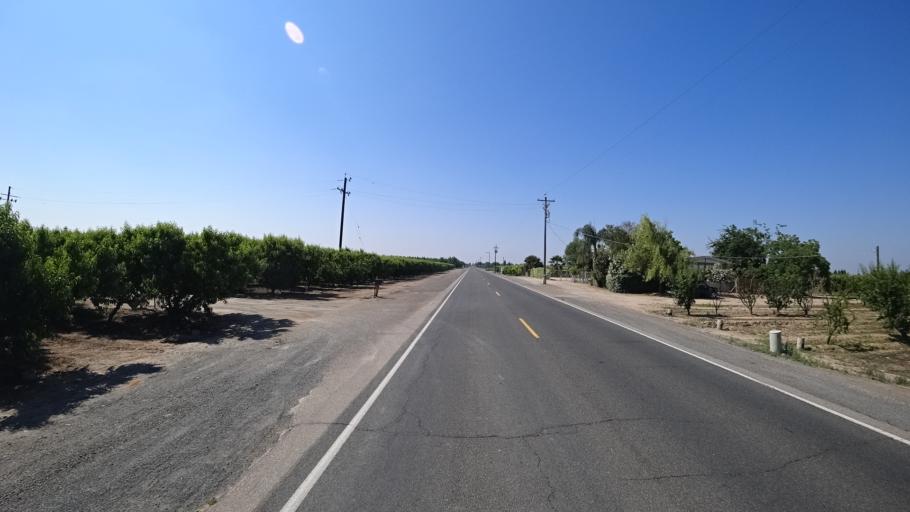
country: US
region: California
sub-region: Fresno County
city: Kingsburg
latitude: 36.4620
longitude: -119.5644
